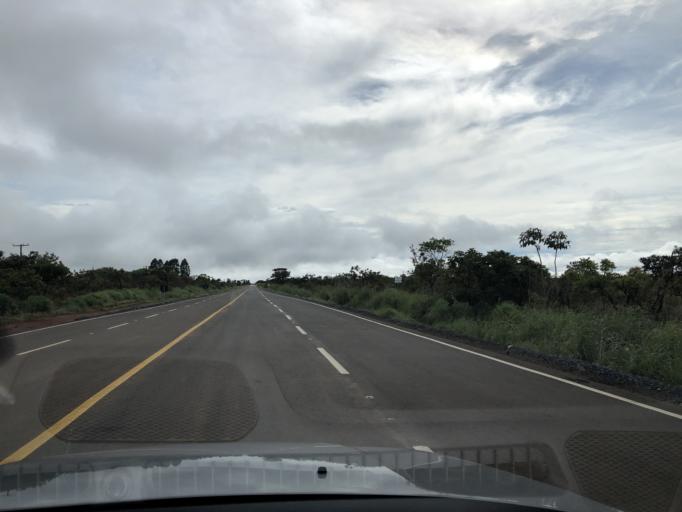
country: BR
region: Federal District
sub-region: Brasilia
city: Brasilia
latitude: -15.6227
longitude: -48.0658
